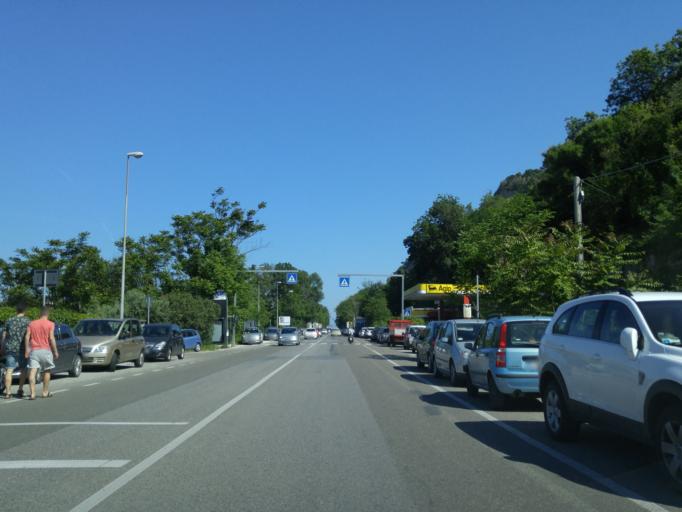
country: IT
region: The Marches
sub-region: Provincia di Pesaro e Urbino
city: Pesaro
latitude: 43.9052
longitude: 12.9268
